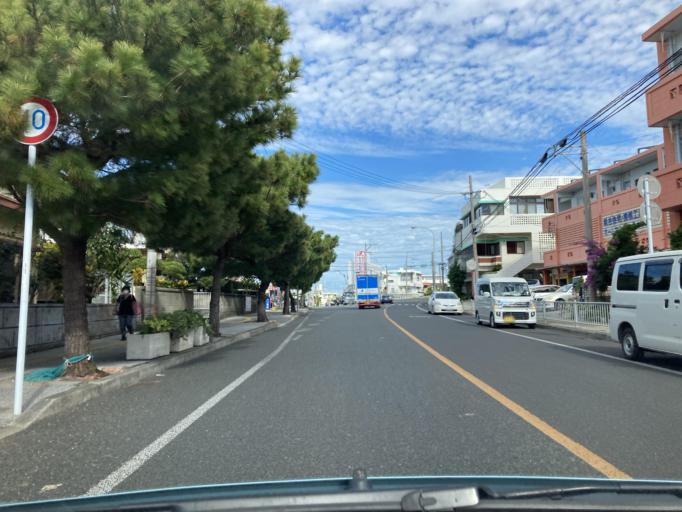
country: JP
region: Okinawa
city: Ishikawa
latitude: 26.3999
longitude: 127.7243
